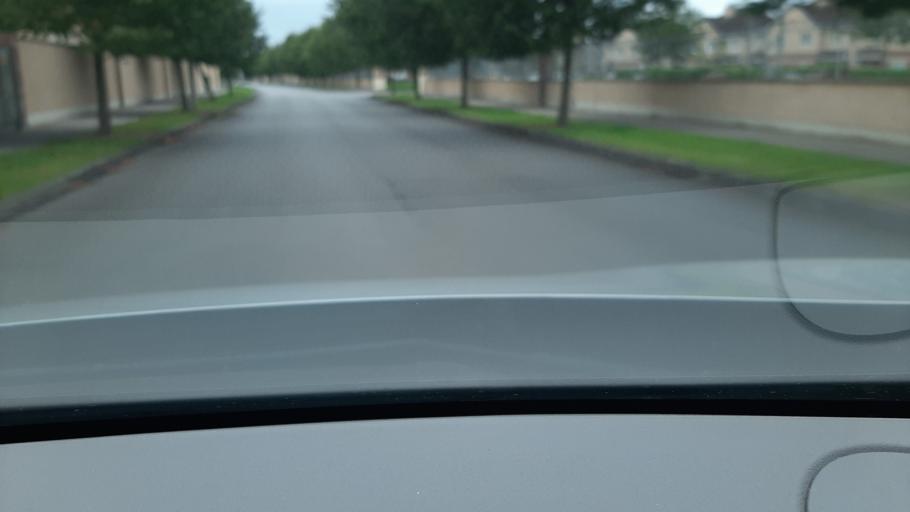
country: IE
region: Leinster
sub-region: Kildare
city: Kildare
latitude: 53.1577
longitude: -6.8968
